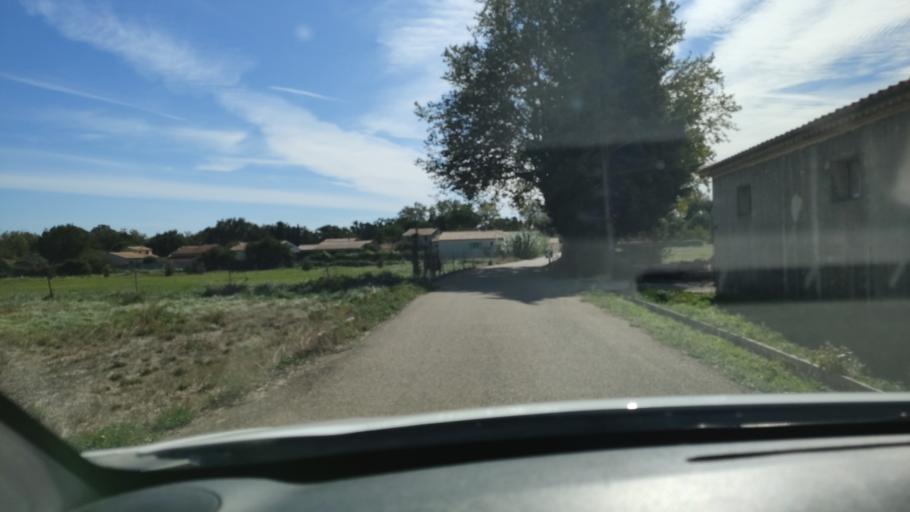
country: FR
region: Provence-Alpes-Cote d'Azur
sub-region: Departement du Vaucluse
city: Morieres-les-Avignon
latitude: 43.9492
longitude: 4.8863
